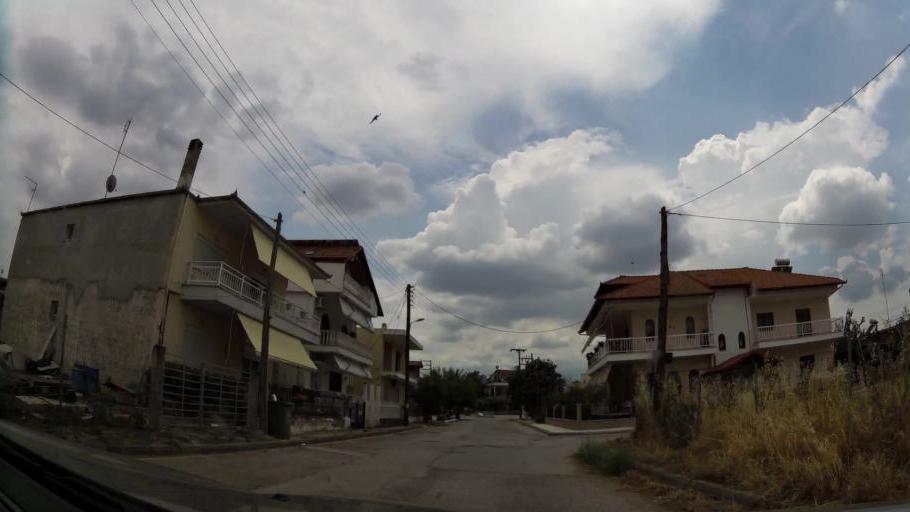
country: GR
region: Central Macedonia
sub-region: Nomos Pierias
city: Kallithea
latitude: 40.2726
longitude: 22.5764
